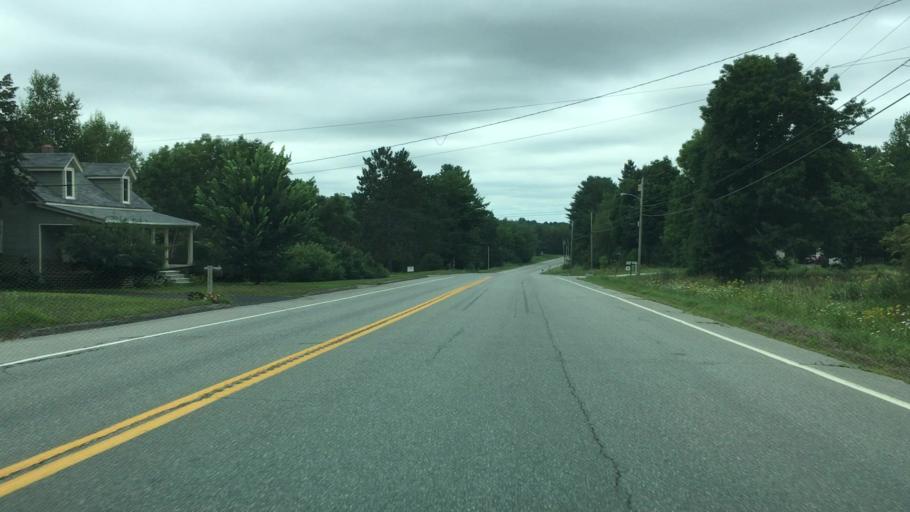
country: US
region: Maine
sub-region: Waldo County
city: Winterport
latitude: 44.6786
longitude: -68.8421
